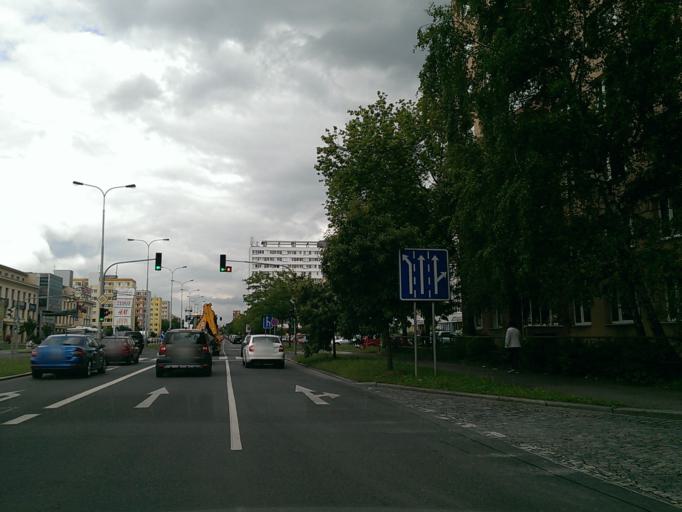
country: CZ
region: Praha
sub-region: Praha 4
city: Hodkovicky
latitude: 50.0265
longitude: 14.4301
